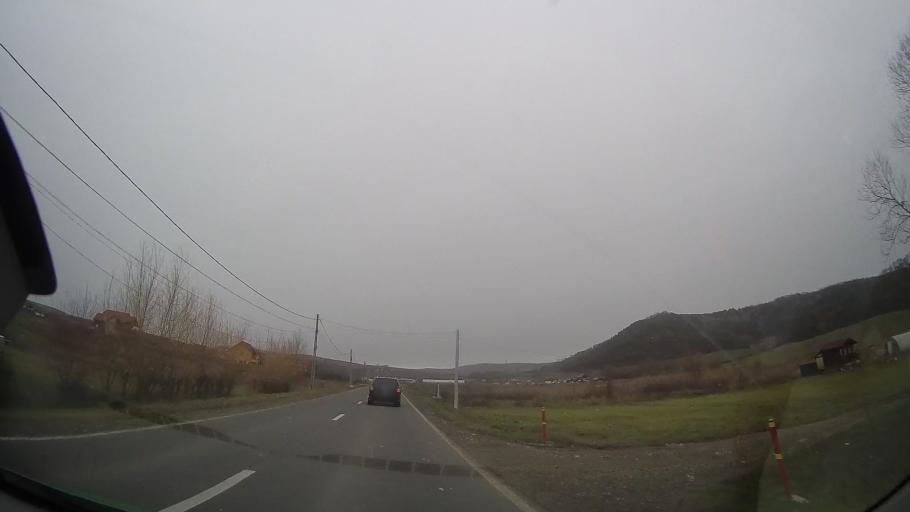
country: RO
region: Mures
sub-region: Comuna Ceausu de Campie
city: Ceausu de Campie
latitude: 46.6294
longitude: 24.5199
